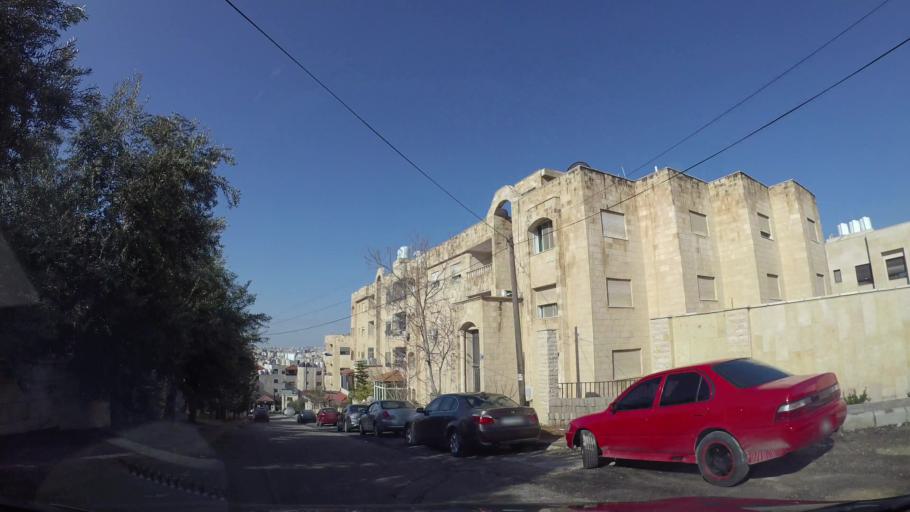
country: JO
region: Amman
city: Al Jubayhah
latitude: 32.0008
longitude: 35.8819
